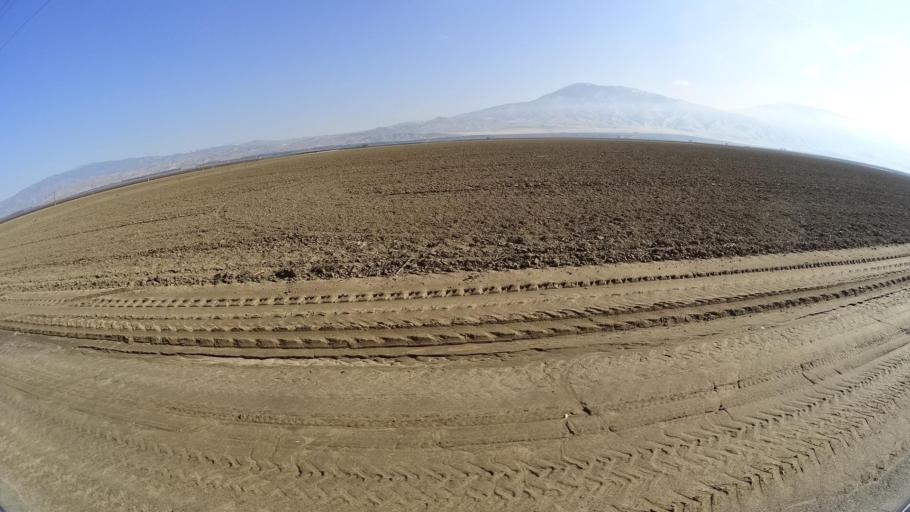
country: US
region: California
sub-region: Kern County
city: Arvin
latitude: 35.2504
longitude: -118.8068
